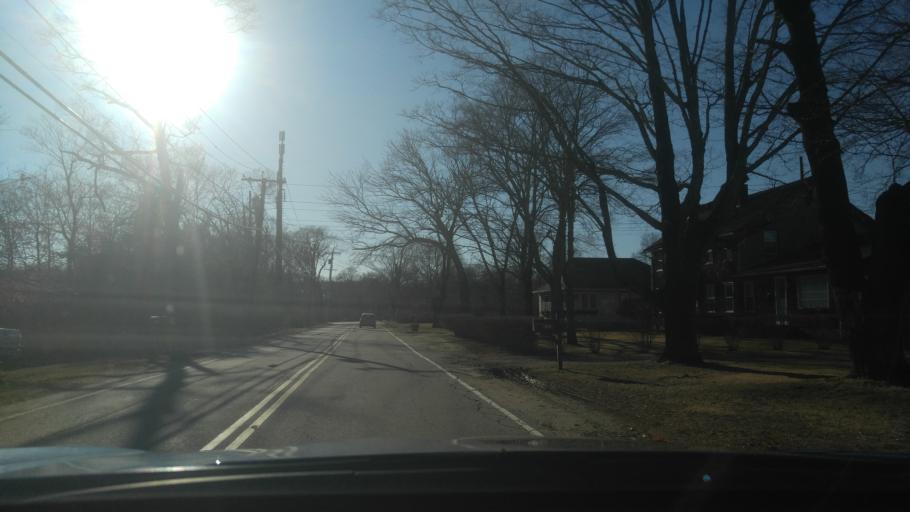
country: US
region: Rhode Island
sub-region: Washington County
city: North Kingstown
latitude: 41.5728
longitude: -71.4904
